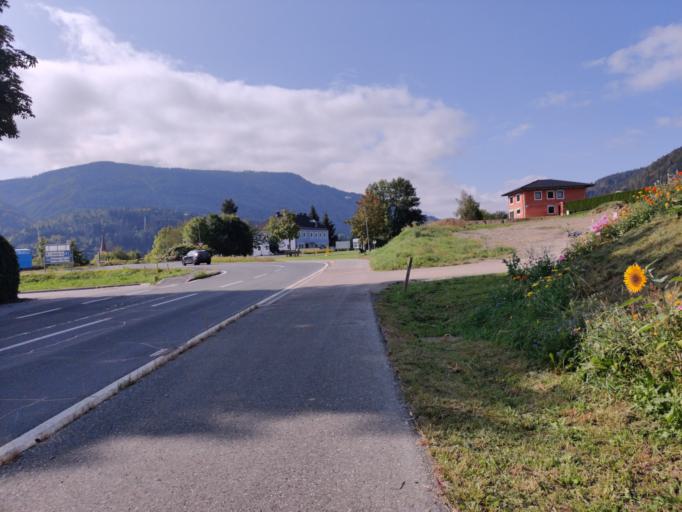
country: AT
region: Carinthia
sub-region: Politischer Bezirk Villach Land
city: Hohenthurn
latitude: 46.5443
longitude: 13.6533
